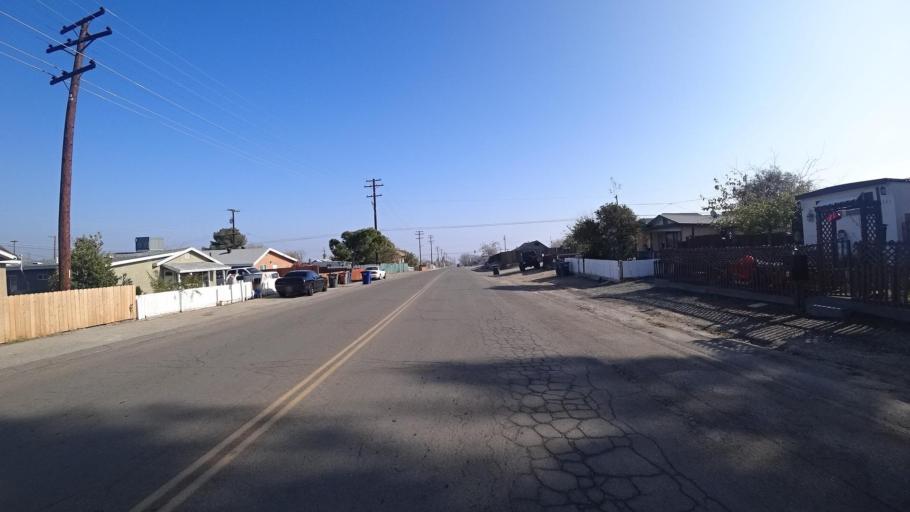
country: US
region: California
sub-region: Kern County
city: South Taft
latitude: 35.1332
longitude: -119.4634
